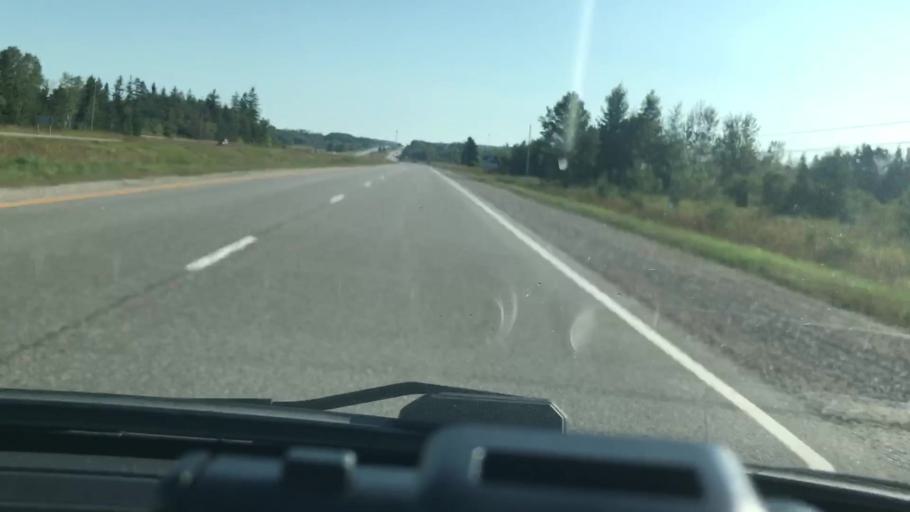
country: CA
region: Ontario
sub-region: Algoma
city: Sault Ste. Marie
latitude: 46.4255
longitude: -84.0683
